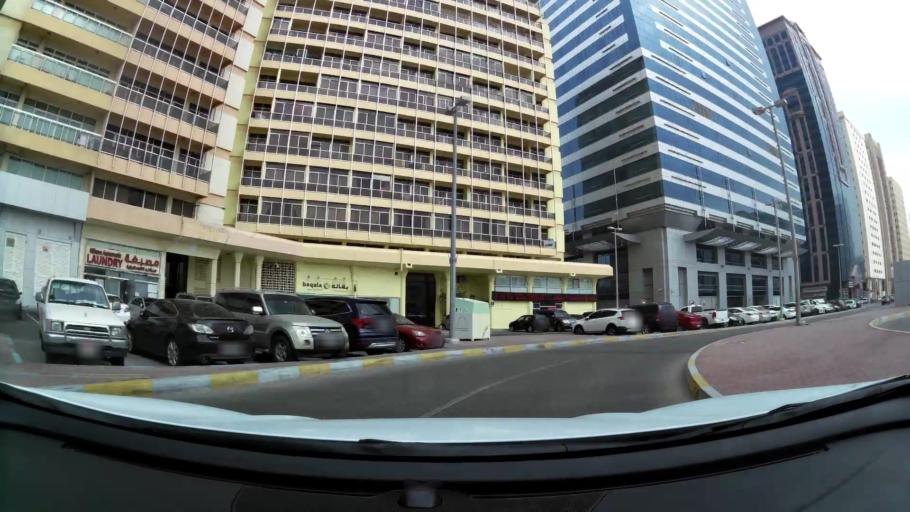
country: AE
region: Abu Dhabi
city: Abu Dhabi
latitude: 24.4827
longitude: 54.3603
